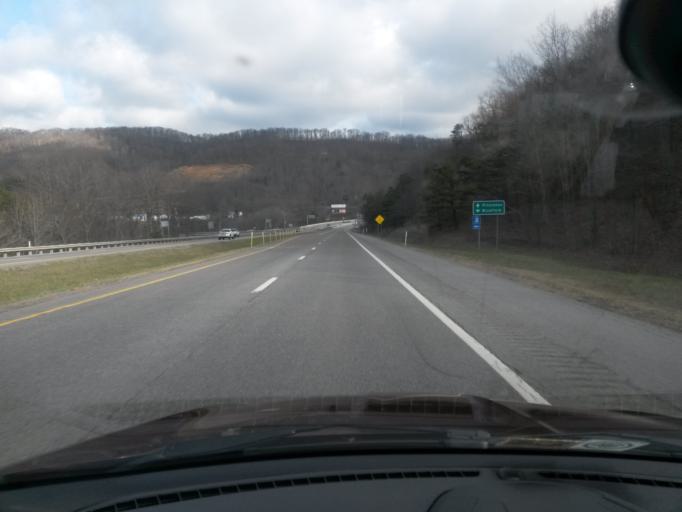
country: US
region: West Virginia
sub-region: Mercer County
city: Bluefield
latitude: 37.2806
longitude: -81.1660
